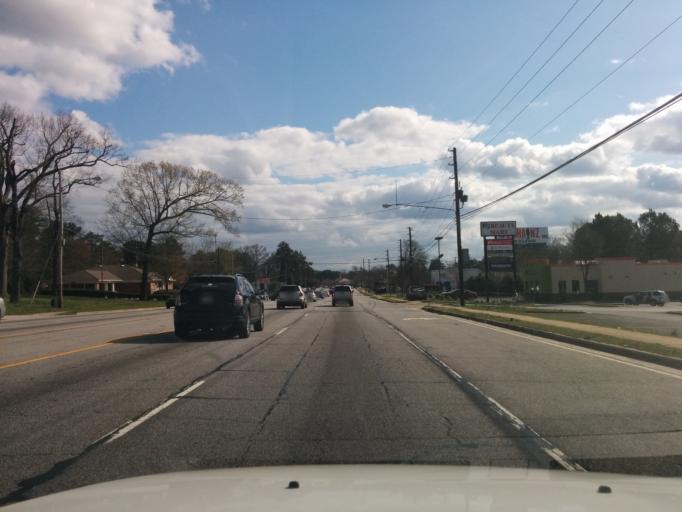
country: US
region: Georgia
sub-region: Fulton County
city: College Park
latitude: 33.6083
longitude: -84.4713
